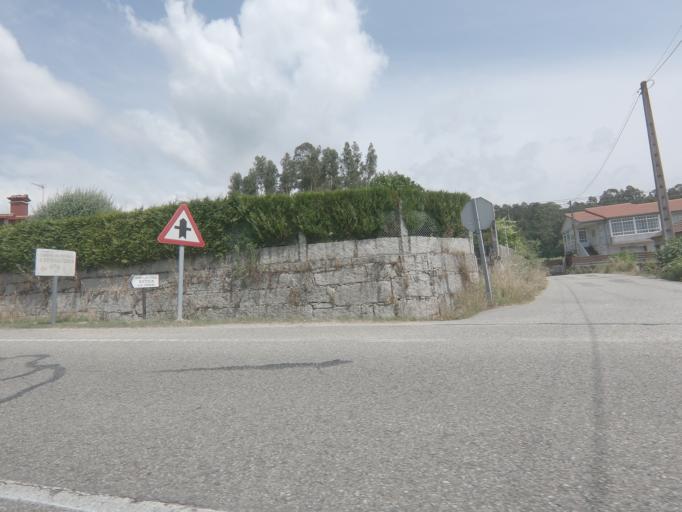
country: ES
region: Galicia
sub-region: Provincia de Pontevedra
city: Tomino
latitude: 42.0320
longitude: -8.7301
